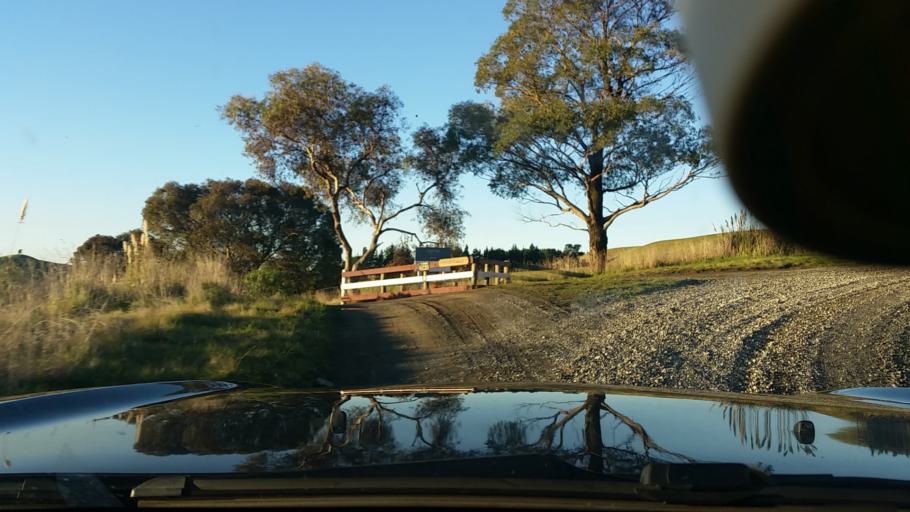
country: NZ
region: Marlborough
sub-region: Marlborough District
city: Blenheim
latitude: -41.7380
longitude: 174.0479
